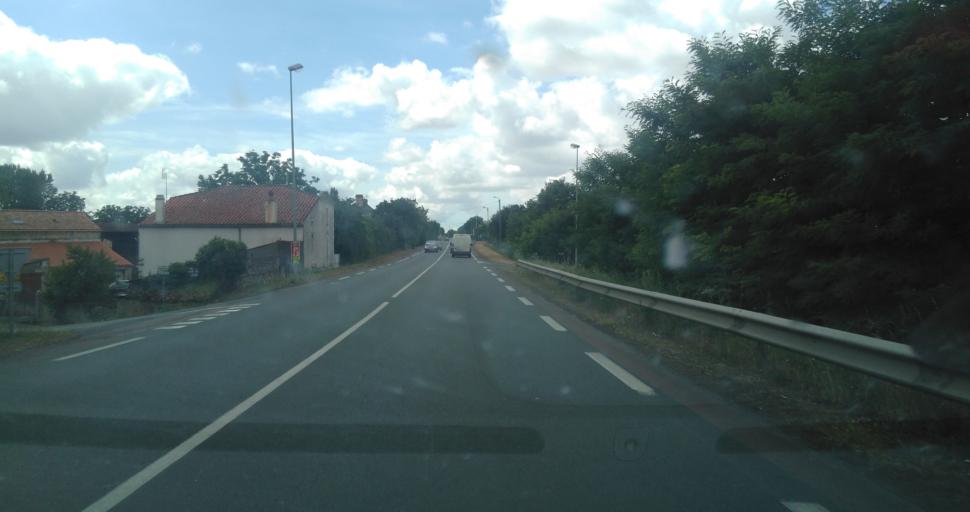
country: FR
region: Pays de la Loire
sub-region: Departement de la Vendee
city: Sainte-Hermine
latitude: 46.5425
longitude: -1.0681
